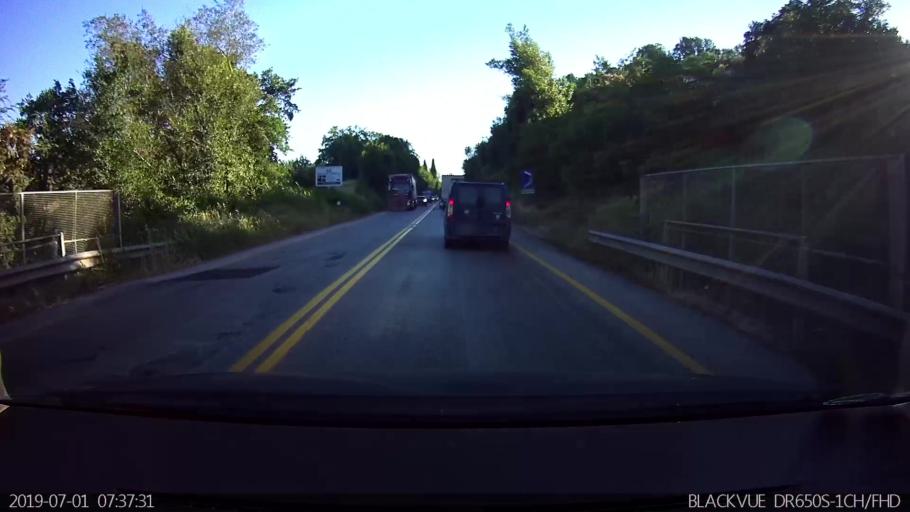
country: IT
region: Latium
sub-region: Provincia di Frosinone
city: Giuliano di Roma
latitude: 41.5384
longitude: 13.2670
